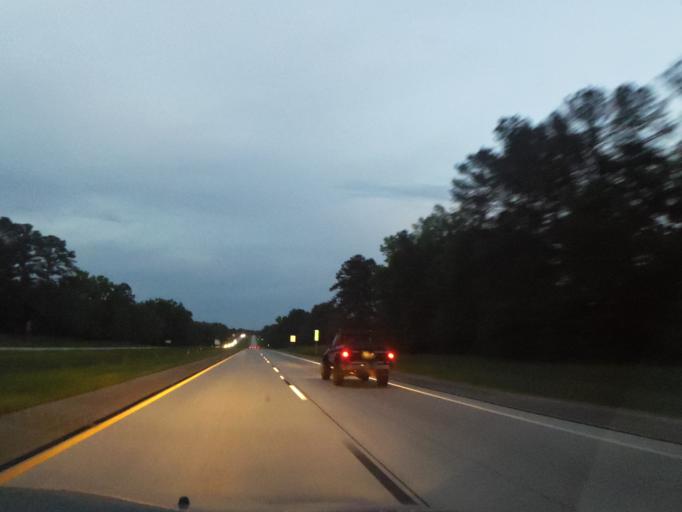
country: US
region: Georgia
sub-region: McDuffie County
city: Thomson
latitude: 33.5121
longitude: -82.4938
